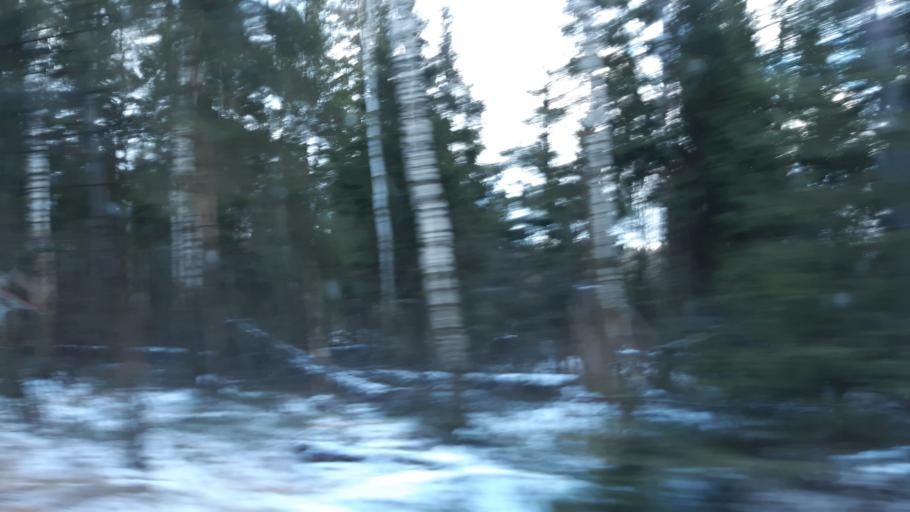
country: RU
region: Moskovskaya
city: Noginsk
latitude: 55.9330
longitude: 38.5445
